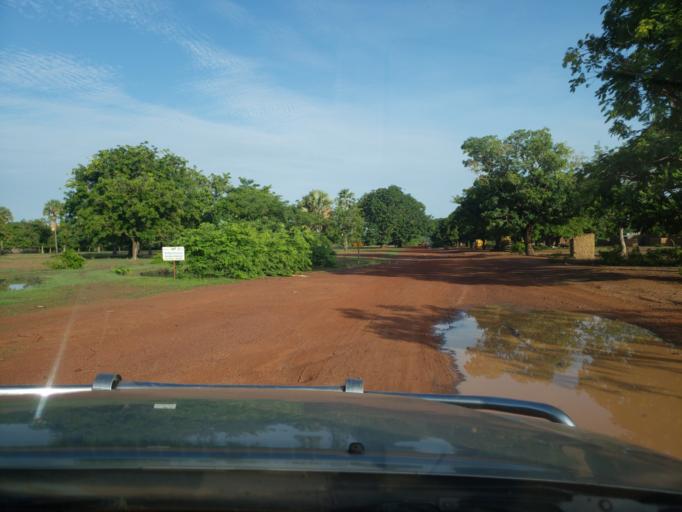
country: ML
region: Sikasso
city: Koutiala
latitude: 12.4210
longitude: -5.5835
